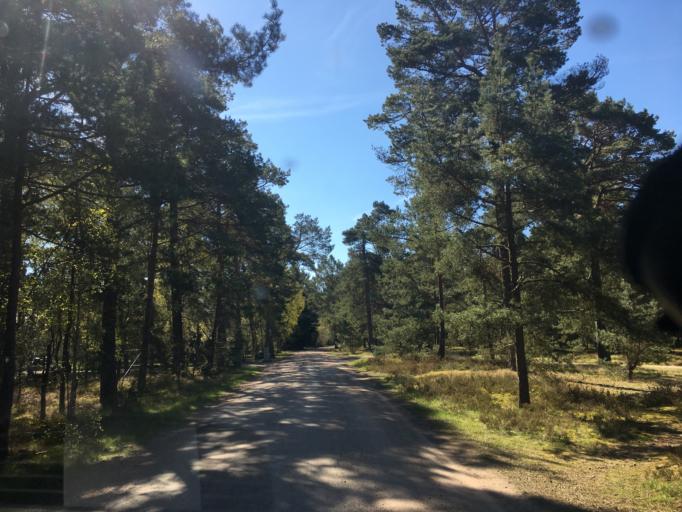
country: SE
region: Skane
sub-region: Vellinge Kommun
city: Ljunghusen
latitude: 55.3980
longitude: 12.9310
